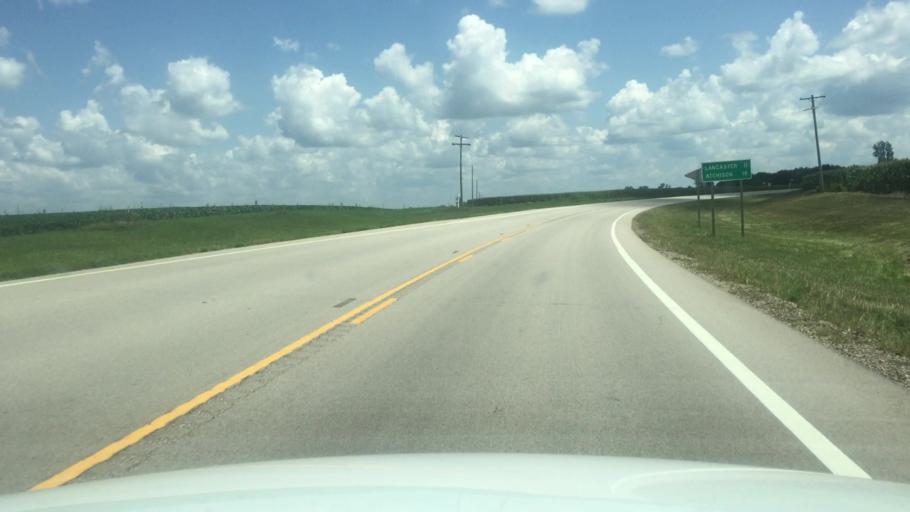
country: US
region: Kansas
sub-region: Brown County
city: Horton
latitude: 39.6674
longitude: -95.4229
